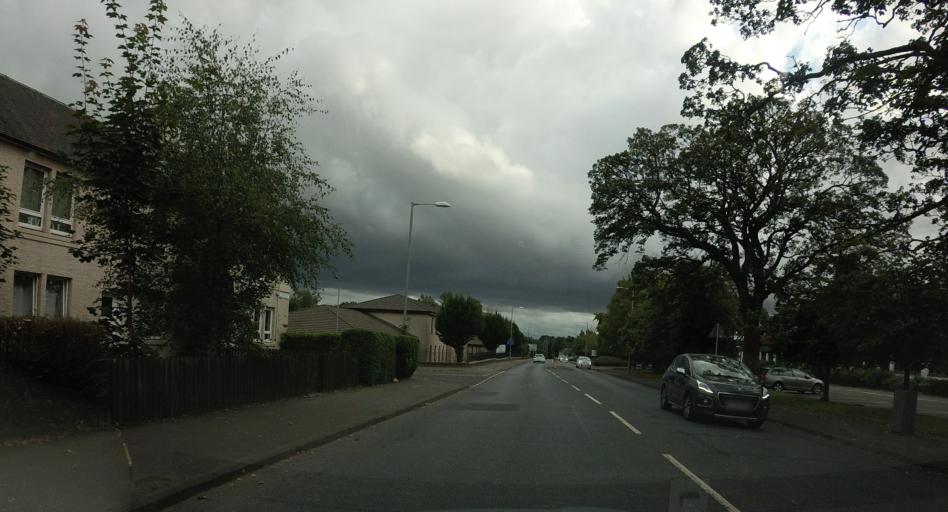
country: GB
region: Scotland
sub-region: Clackmannanshire
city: Alloa
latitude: 56.1227
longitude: -3.7808
